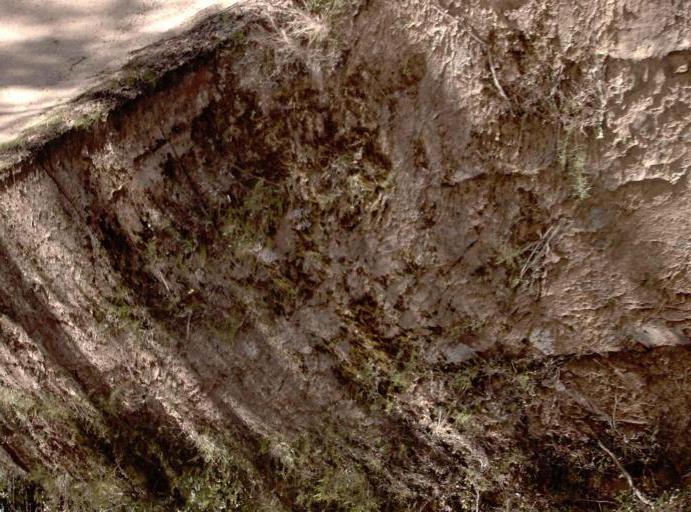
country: AU
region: New South Wales
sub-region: Bombala
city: Bombala
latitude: -37.5922
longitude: 148.9784
